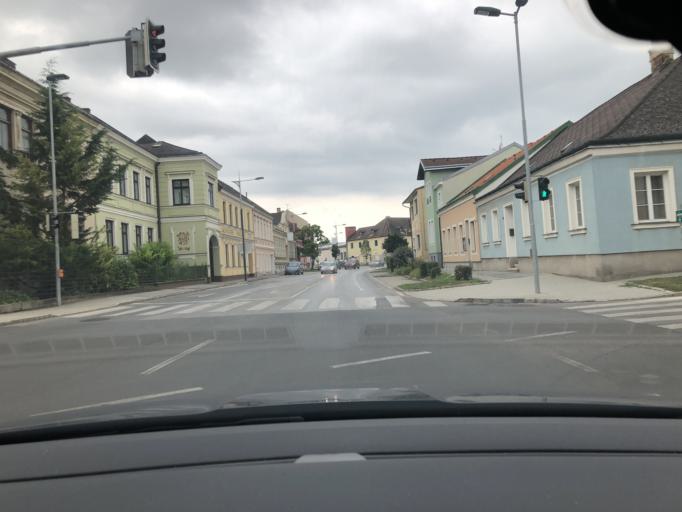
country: AT
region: Lower Austria
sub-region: Politischer Bezirk Mistelbach
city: Laa an der Thaya
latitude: 48.7185
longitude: 16.3911
